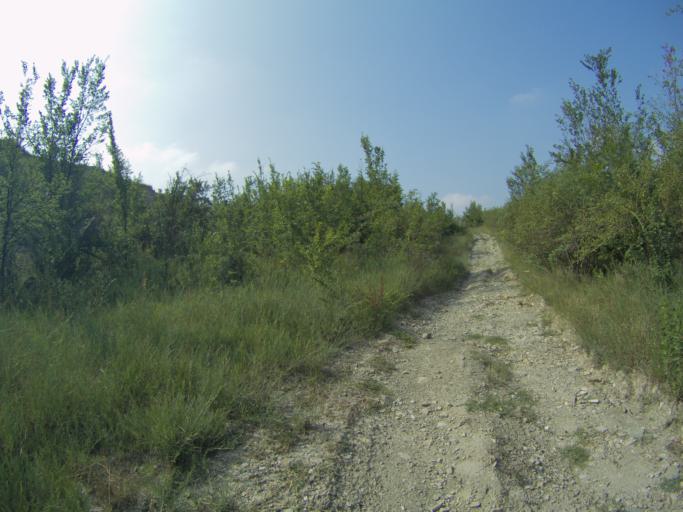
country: IT
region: Emilia-Romagna
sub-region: Provincia di Reggio Emilia
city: Ventoso
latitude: 44.5764
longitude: 10.6574
